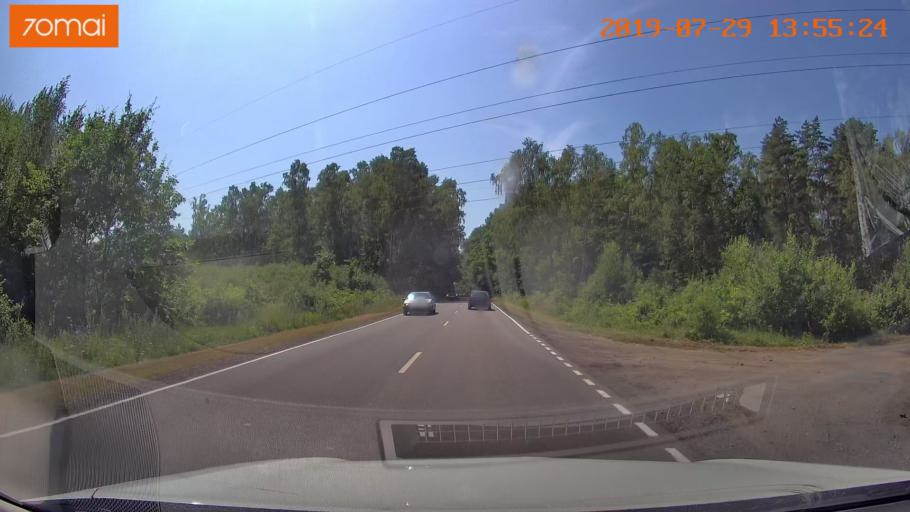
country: RU
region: Kaliningrad
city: Primorsk
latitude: 54.7155
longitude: 19.9573
